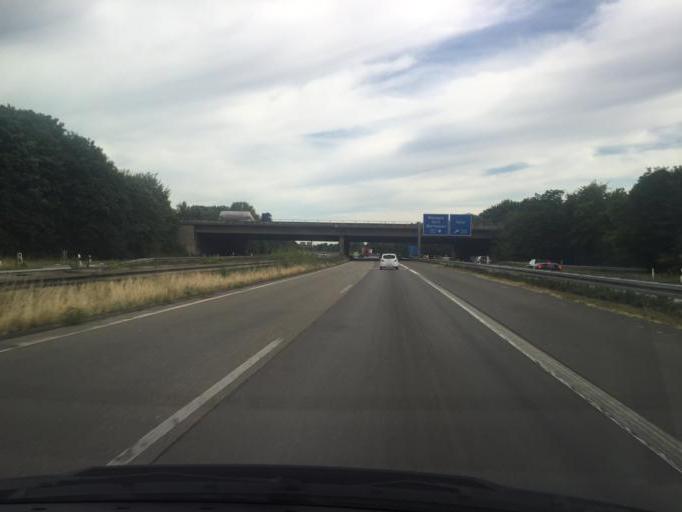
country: DE
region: North Rhine-Westphalia
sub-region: Regierungsbezirk Dusseldorf
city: Moers
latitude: 51.4348
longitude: 6.6047
